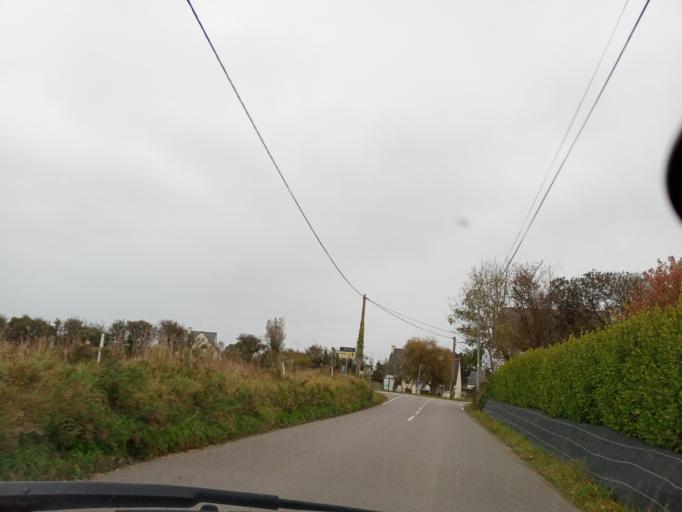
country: FR
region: Brittany
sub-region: Departement du Finistere
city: Esquibien
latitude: 48.0203
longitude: -4.5638
